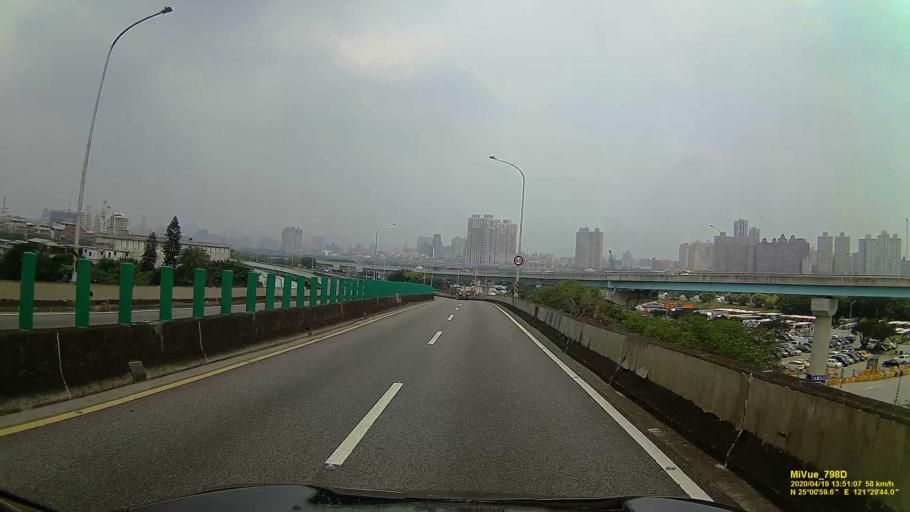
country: TW
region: Taipei
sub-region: Taipei
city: Banqiao
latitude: 25.0165
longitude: 121.4958
